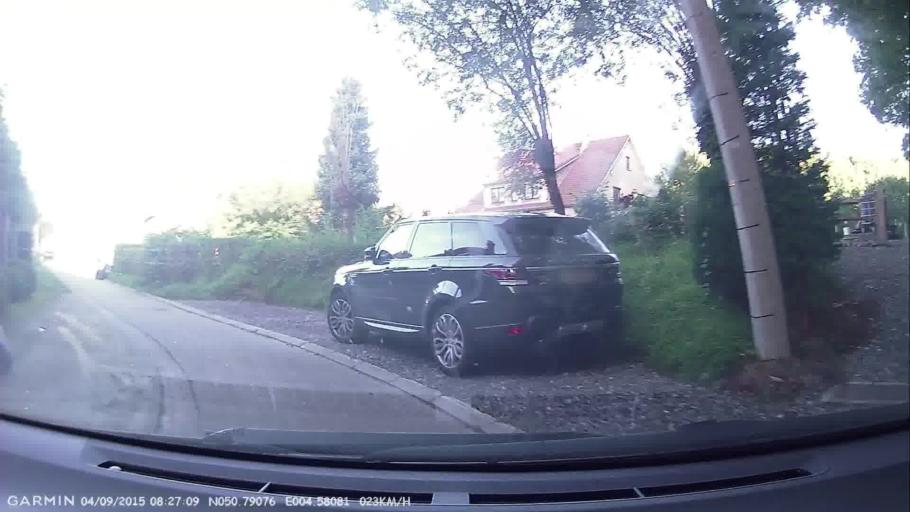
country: BE
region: Flanders
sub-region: Provincie Vlaams-Brabant
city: Huldenberg
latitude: 50.7908
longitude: 4.5807
